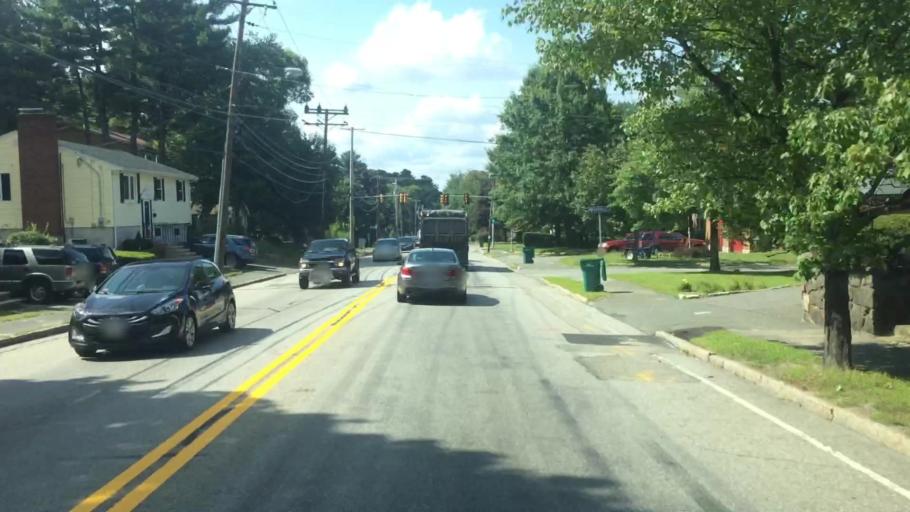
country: US
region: Massachusetts
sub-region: Essex County
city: South Peabody
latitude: 42.5054
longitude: -70.9820
